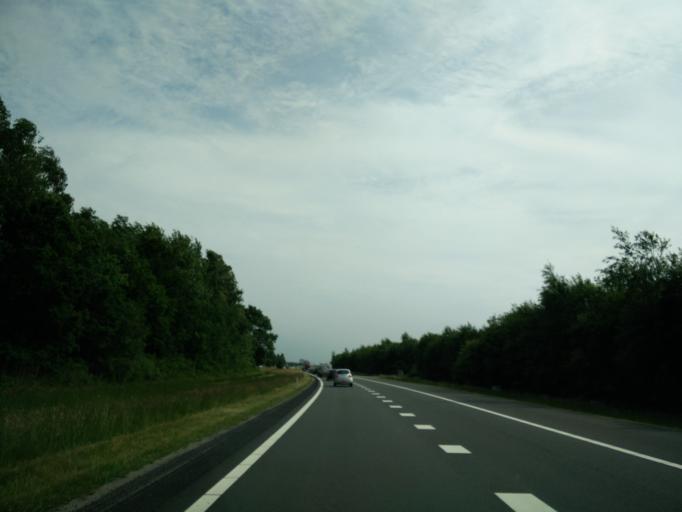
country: NL
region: Drenthe
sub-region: Gemeente Assen
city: Assen
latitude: 52.9652
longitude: 6.5457
